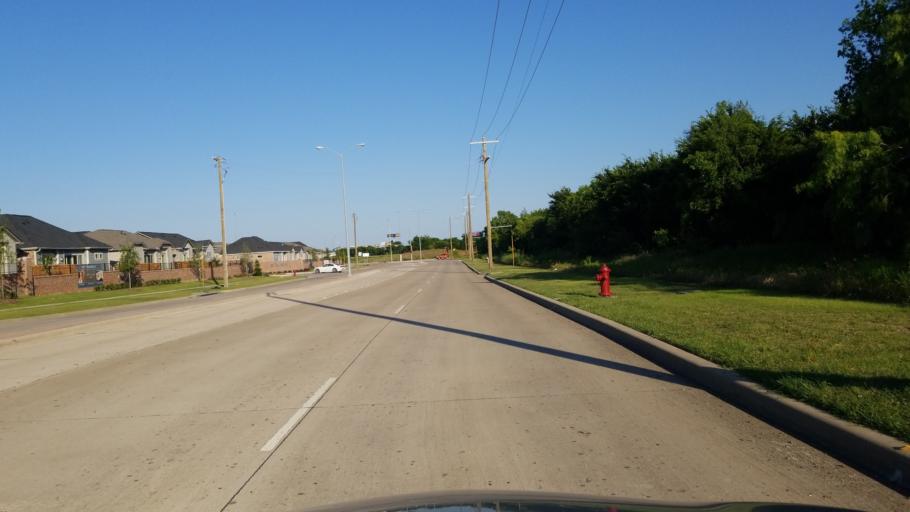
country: US
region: Texas
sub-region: Dallas County
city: Grand Prairie
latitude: 32.6831
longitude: -97.0309
